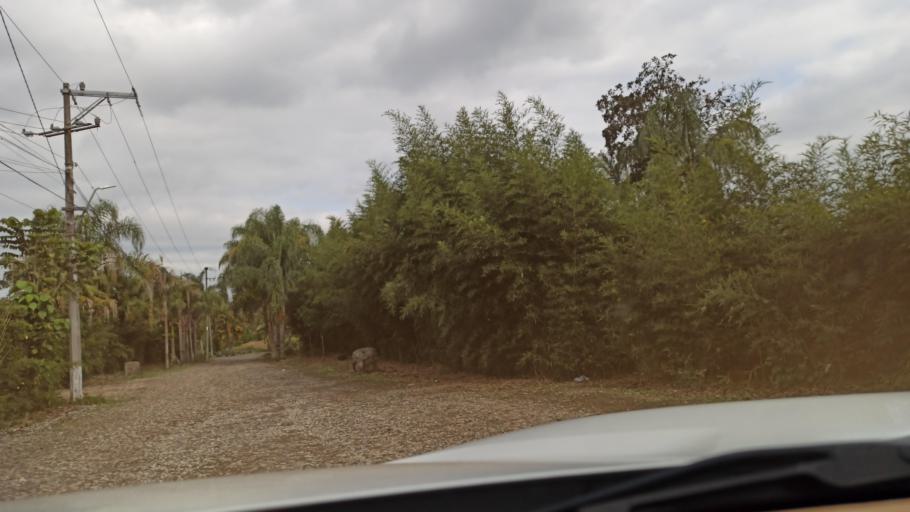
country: MX
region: Veracruz
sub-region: Fortin
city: Fortin de las Flores
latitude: 18.9024
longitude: -96.9927
